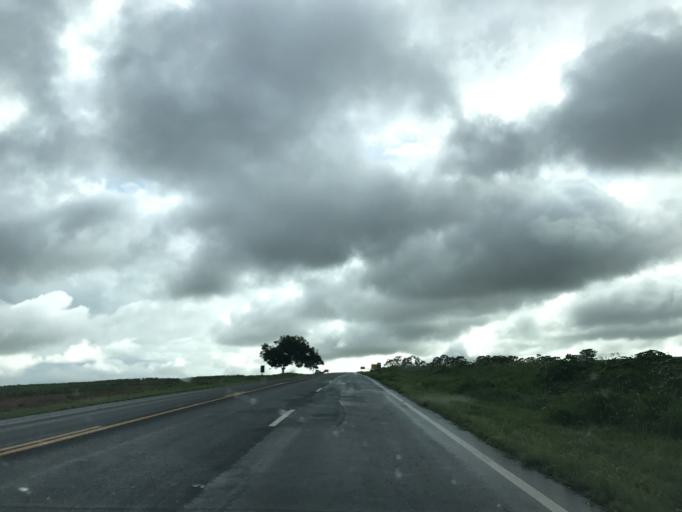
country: BR
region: Sao Paulo
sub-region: Penapolis
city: Penapolis
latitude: -21.4988
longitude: -50.2504
